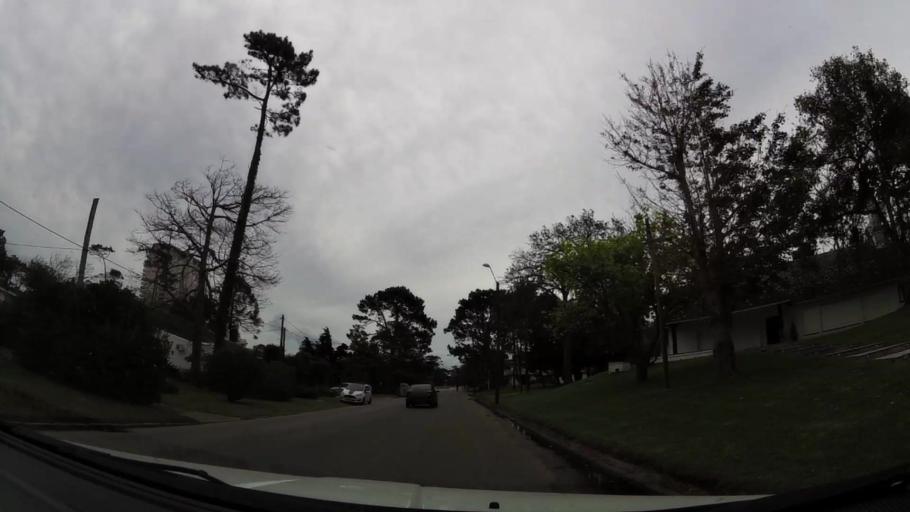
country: UY
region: Maldonado
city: Maldonado
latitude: -34.9316
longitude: -54.9520
